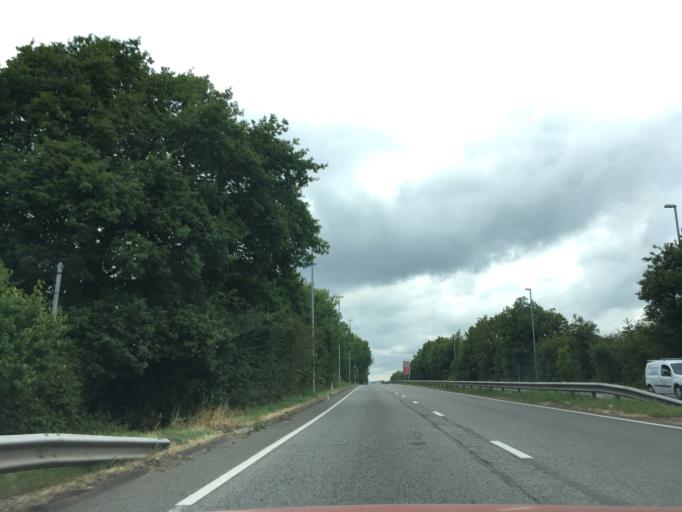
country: GB
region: Wales
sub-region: Torfaen County Borough
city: Cwmbran
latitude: 51.6610
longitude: -3.0003
